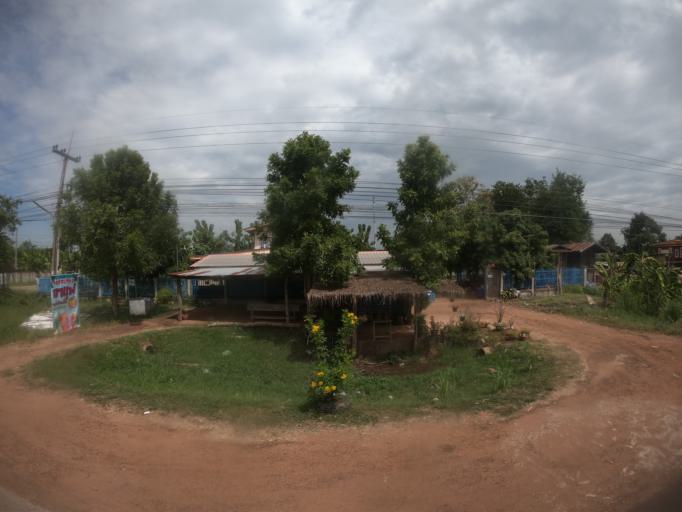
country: TH
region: Maha Sarakham
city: Chiang Yuen
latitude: 16.3430
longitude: 103.1517
